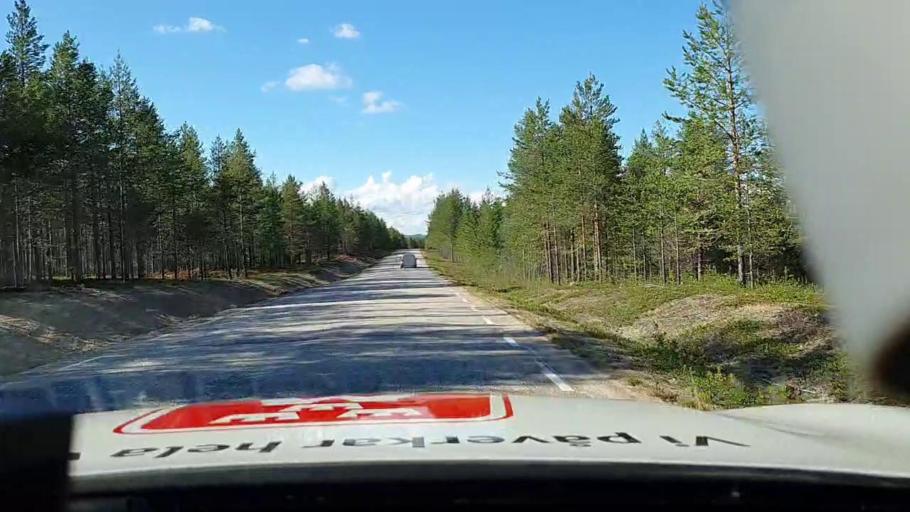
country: SE
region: Norrbotten
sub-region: Overkalix Kommun
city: OEverkalix
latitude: 66.2387
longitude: 22.9308
